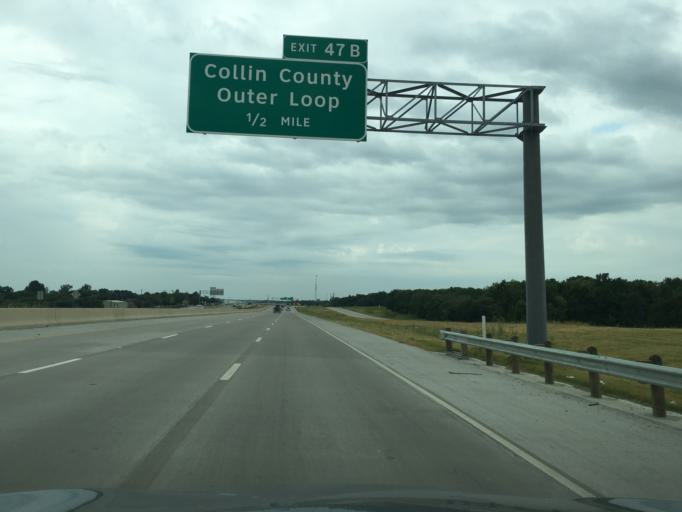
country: US
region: Texas
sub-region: Collin County
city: Anna
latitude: 33.3332
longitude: -96.5890
